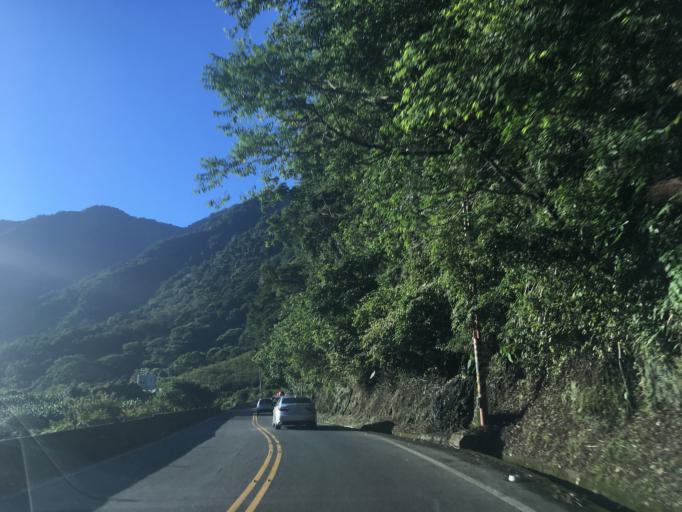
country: TW
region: Taiwan
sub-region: Nantou
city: Puli
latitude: 23.9965
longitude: 121.0696
